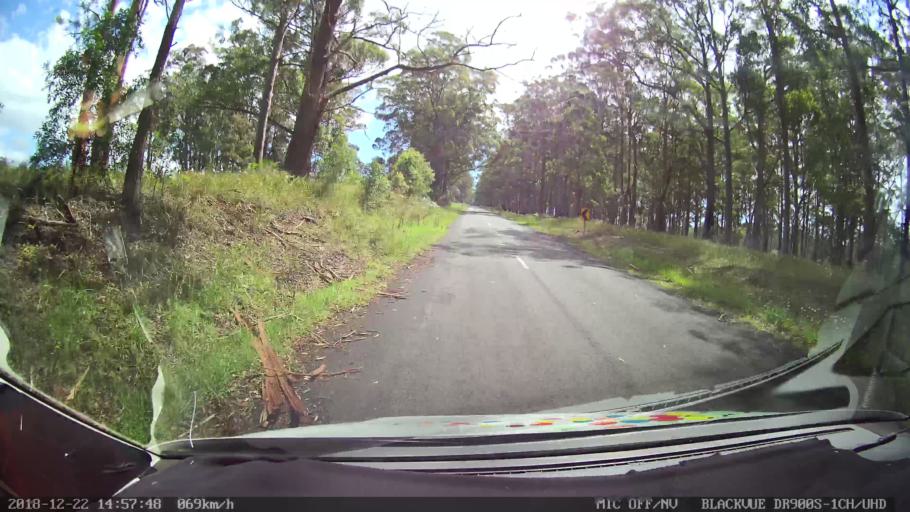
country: AU
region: New South Wales
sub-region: Bellingen
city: Dorrigo
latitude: -30.2364
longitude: 152.4972
